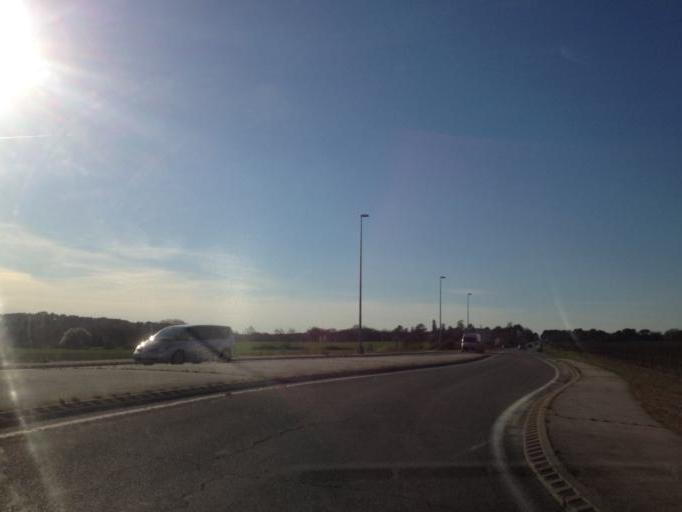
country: FR
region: Provence-Alpes-Cote d'Azur
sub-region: Departement des Bouches-du-Rhone
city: Eguilles
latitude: 43.5865
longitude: 5.3691
